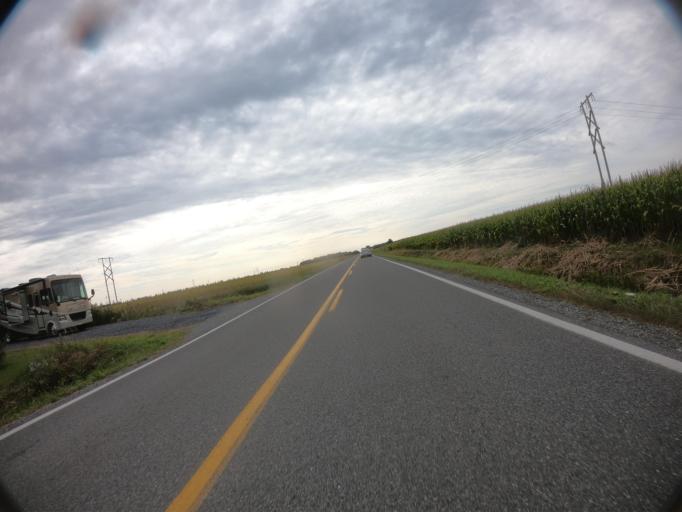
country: CA
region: Quebec
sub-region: Monteregie
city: Marieville
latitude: 45.4273
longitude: -73.1831
